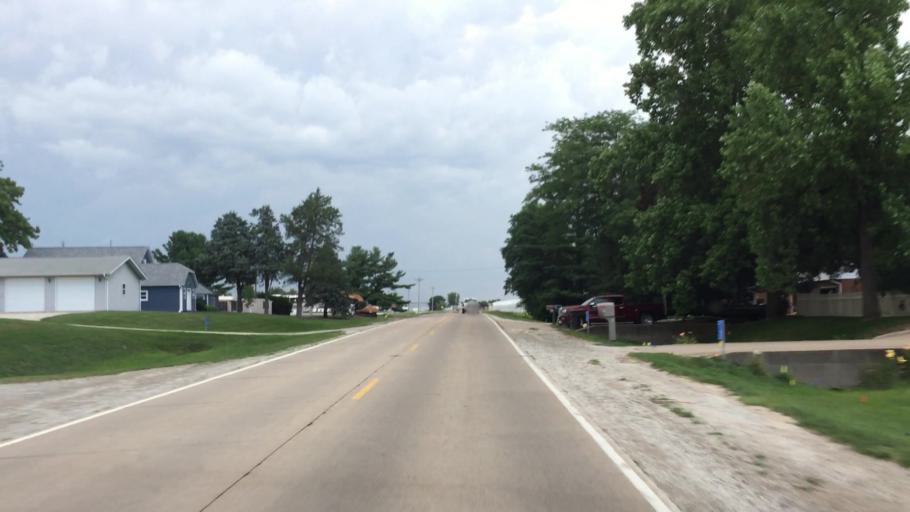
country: US
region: Iowa
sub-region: Lee County
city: Fort Madison
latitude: 40.6481
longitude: -91.3173
